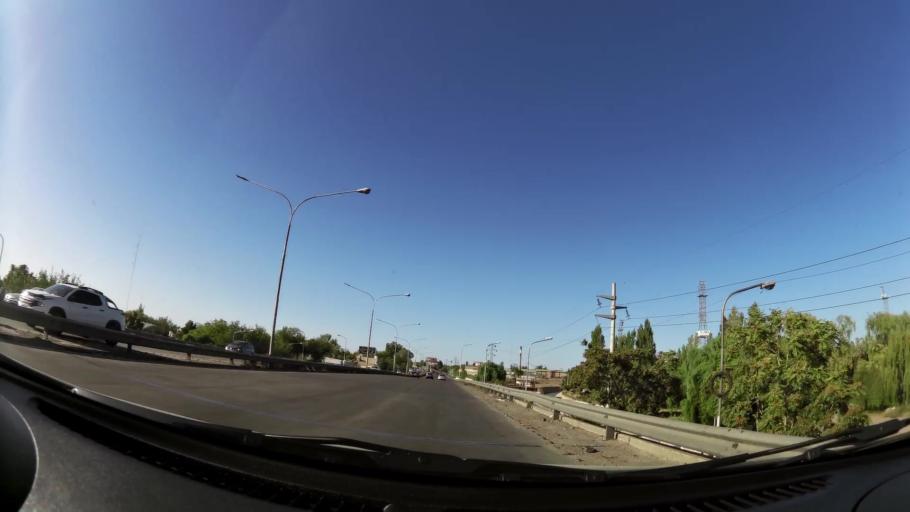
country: AR
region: Mendoza
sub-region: Departamento de Godoy Cruz
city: Godoy Cruz
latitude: -32.9189
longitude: -68.8376
